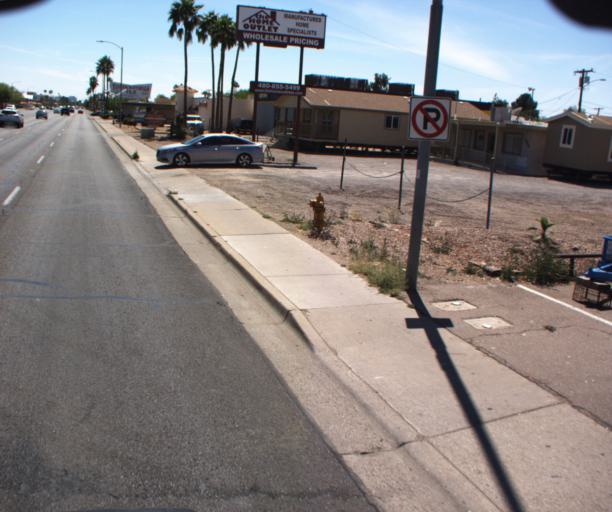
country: US
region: Arizona
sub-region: Maricopa County
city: Chandler
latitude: 33.3191
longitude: -111.8417
